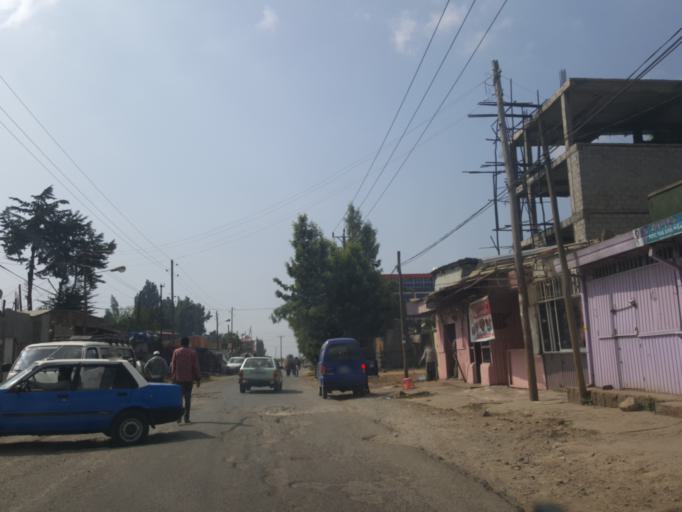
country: ET
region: Adis Abeba
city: Addis Ababa
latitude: 9.0609
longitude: 38.7195
